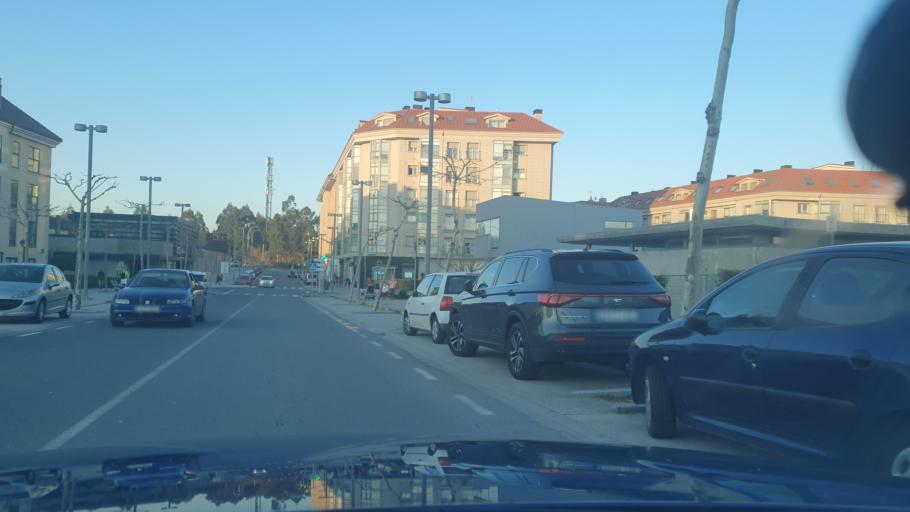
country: ES
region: Galicia
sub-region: Provincia da Coruna
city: Santiago de Compostela
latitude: 42.8467
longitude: -8.5803
